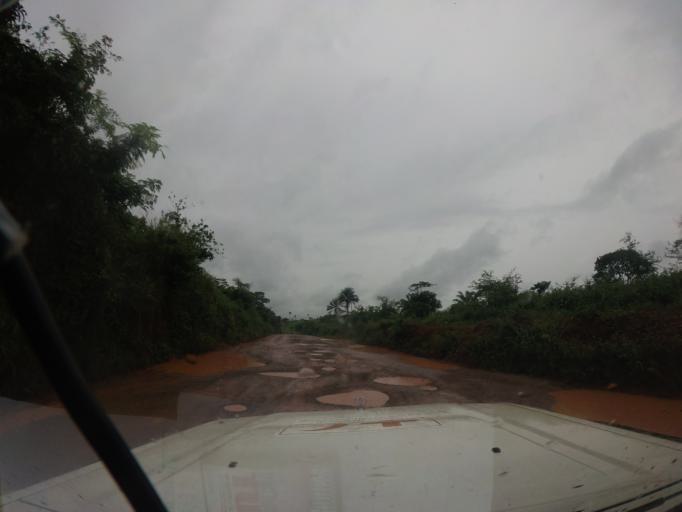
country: SL
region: Eastern Province
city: Tefeya
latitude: 8.5735
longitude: -11.3121
